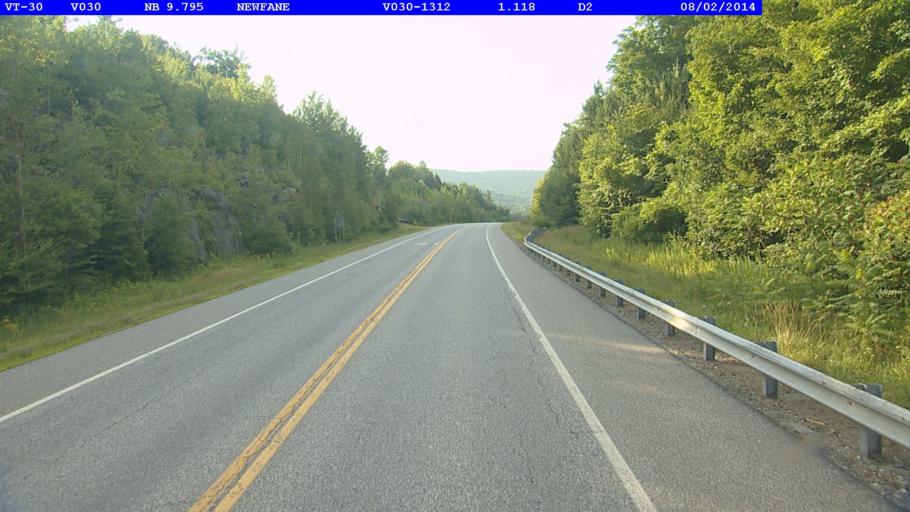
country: US
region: Vermont
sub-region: Windham County
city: Newfane
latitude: 42.9611
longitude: -72.6524
